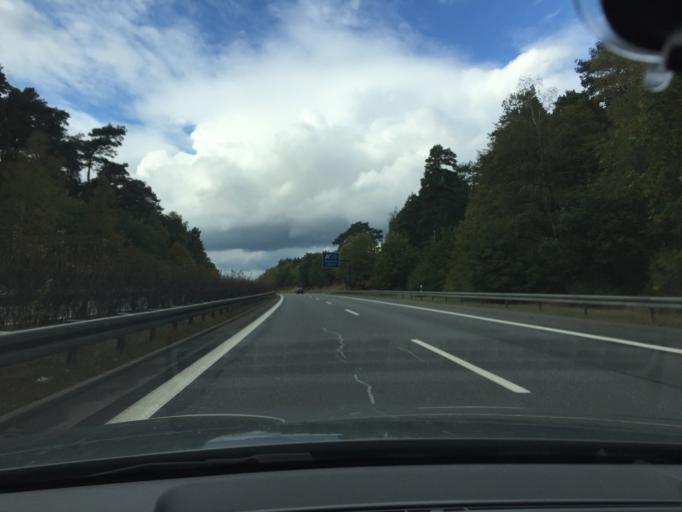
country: DE
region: Brandenburg
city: Bronkow
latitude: 51.6587
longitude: 13.9286
